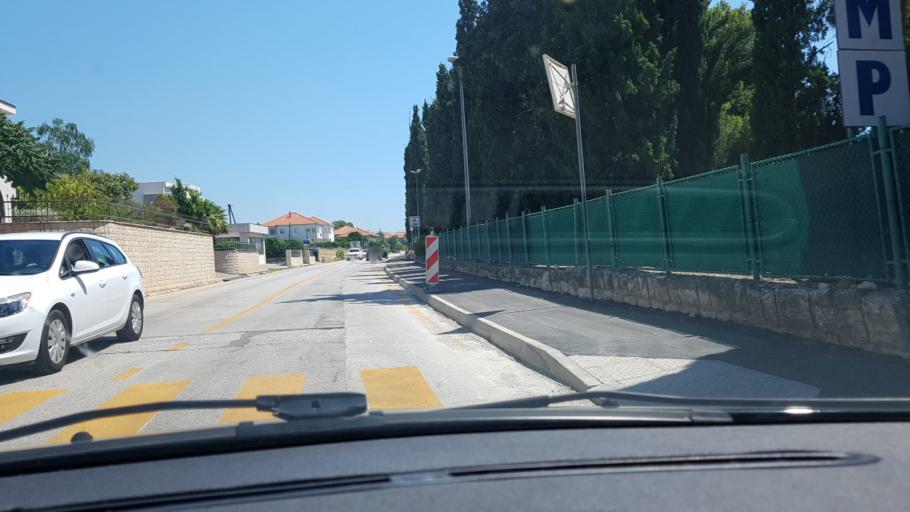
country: HR
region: Splitsko-Dalmatinska
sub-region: Grad Trogir
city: Trogir
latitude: 43.5190
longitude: 16.2235
